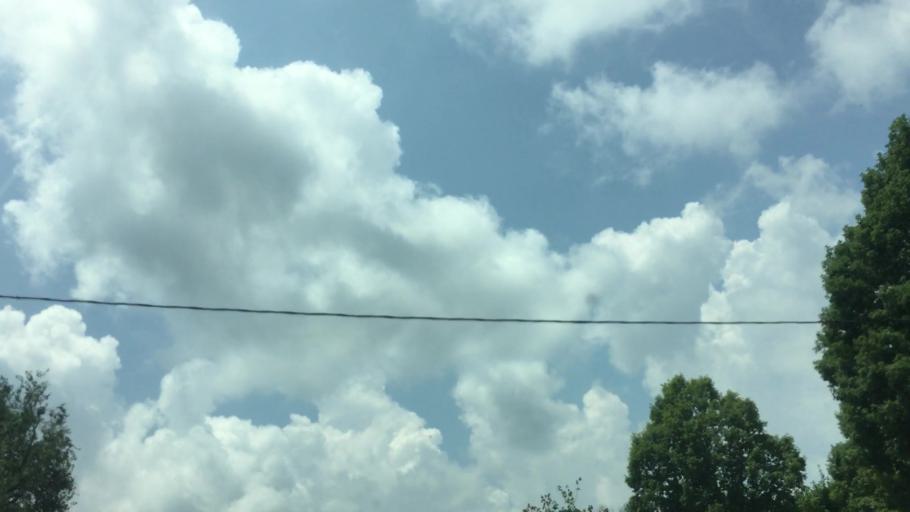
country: US
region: Georgia
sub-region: Fulton County
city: Chattahoochee Hills
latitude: 33.6195
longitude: -84.8503
